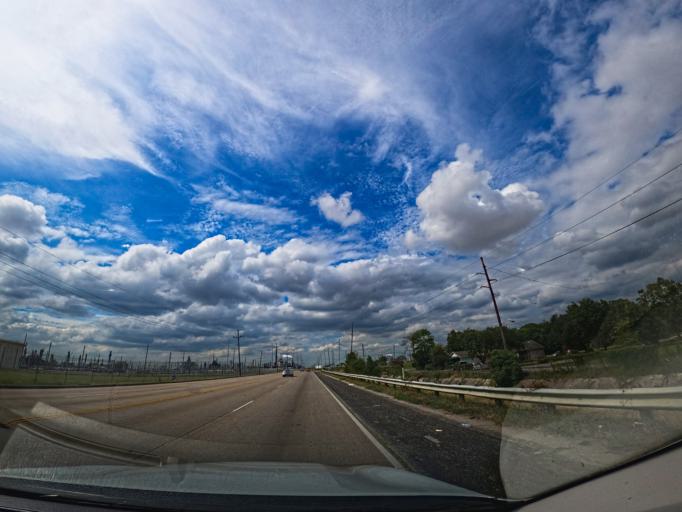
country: US
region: Texas
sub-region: Jefferson County
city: Port Arthur
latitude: 29.8606
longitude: -93.9550
